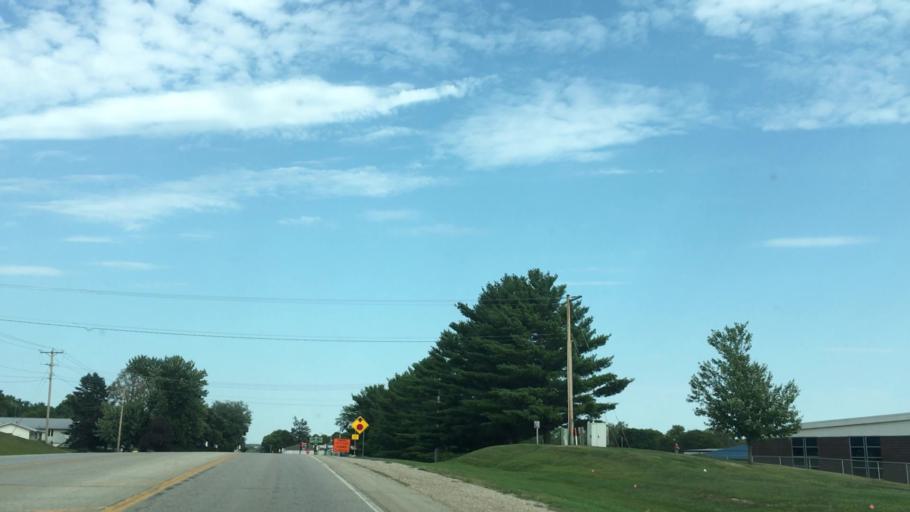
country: US
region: Iowa
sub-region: Johnson County
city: Tiffin
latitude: 41.7080
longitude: -91.6697
